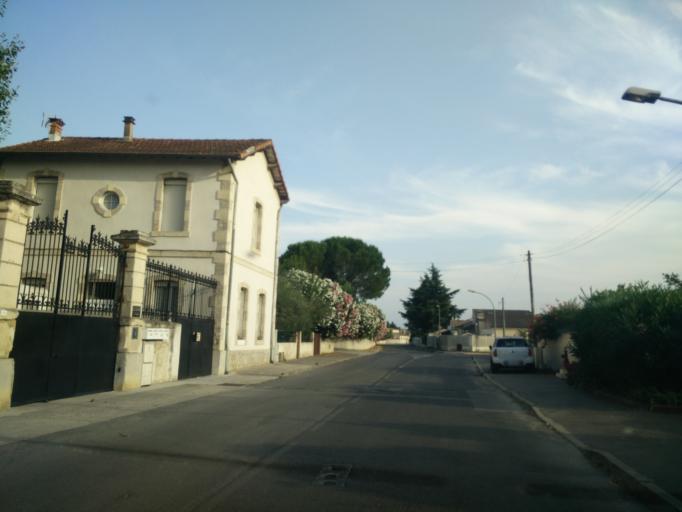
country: FR
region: Languedoc-Roussillon
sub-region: Departement de l'Herault
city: Marsillargues
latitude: 43.6626
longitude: 4.1712
